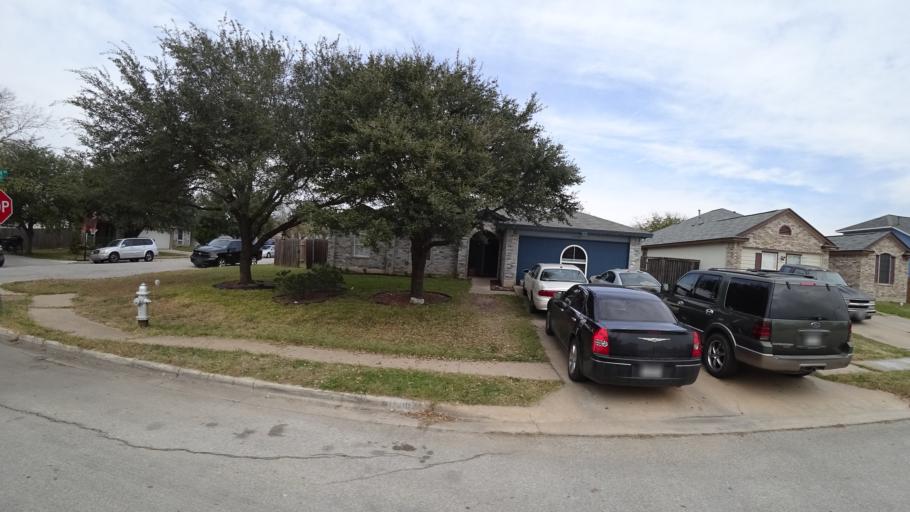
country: US
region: Texas
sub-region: Travis County
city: Garfield
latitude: 30.1559
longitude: -97.6467
